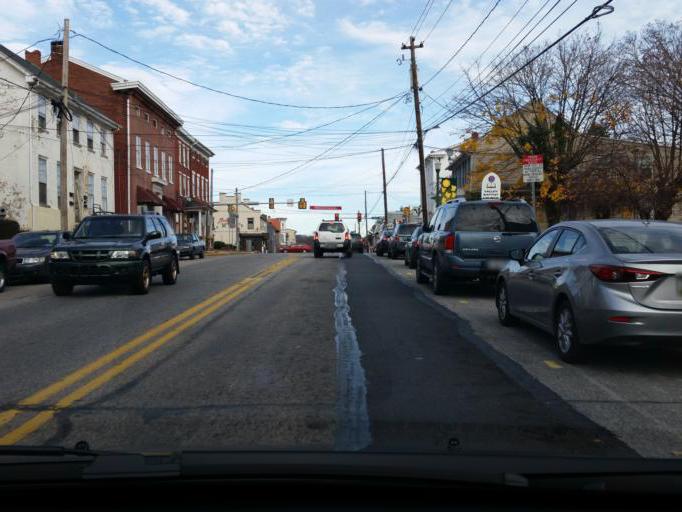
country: US
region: Pennsylvania
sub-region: Dauphin County
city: Middletown
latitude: 40.1994
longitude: -76.7323
